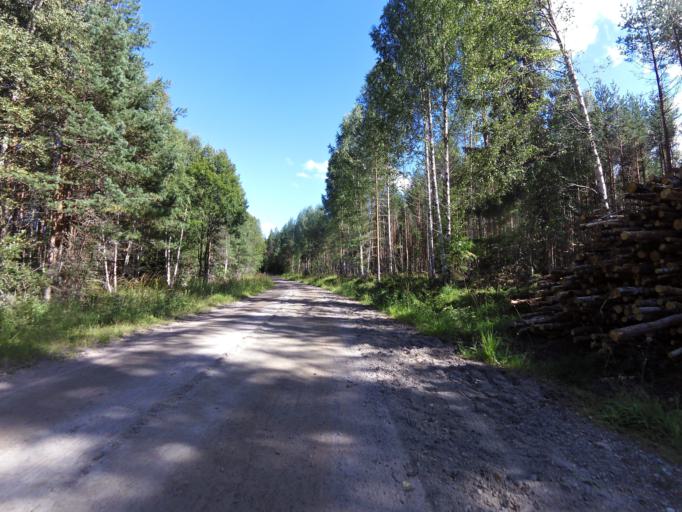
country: SE
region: Gaevleborg
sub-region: Hofors Kommun
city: Hofors
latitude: 60.5035
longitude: 16.3668
